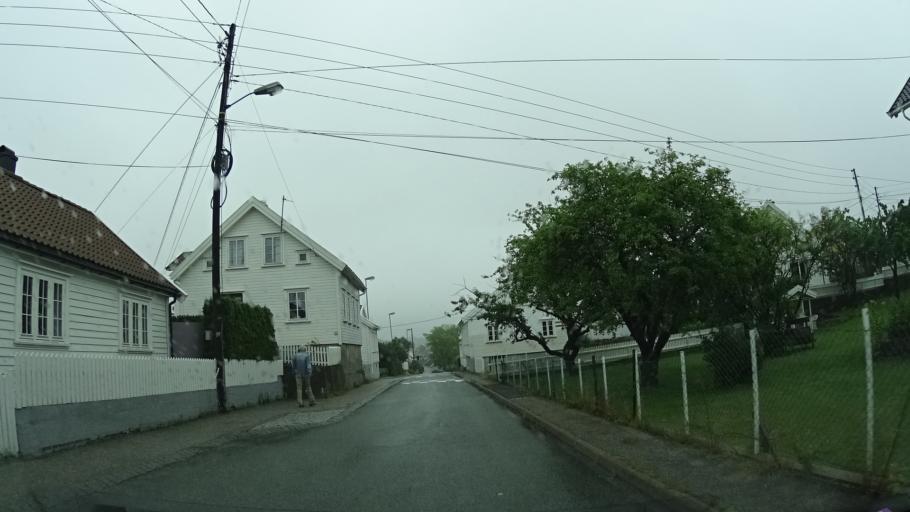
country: NO
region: Aust-Agder
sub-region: Lillesand
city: Lillesand
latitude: 58.2460
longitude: 8.3753
